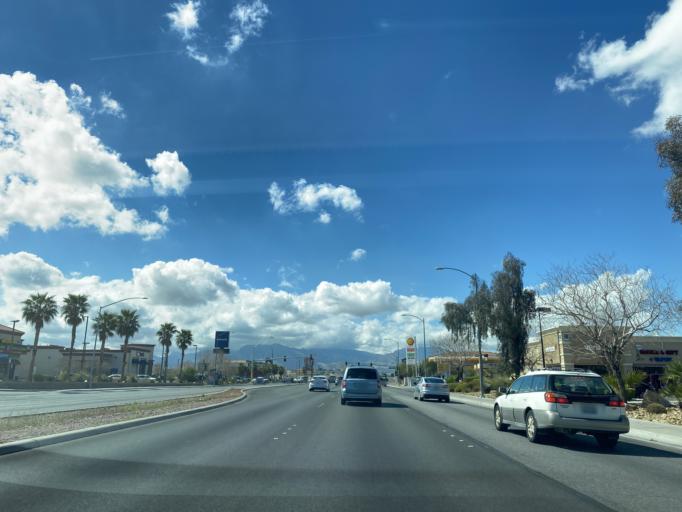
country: US
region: Nevada
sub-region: Clark County
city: Las Vegas
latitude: 36.2391
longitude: -115.2236
